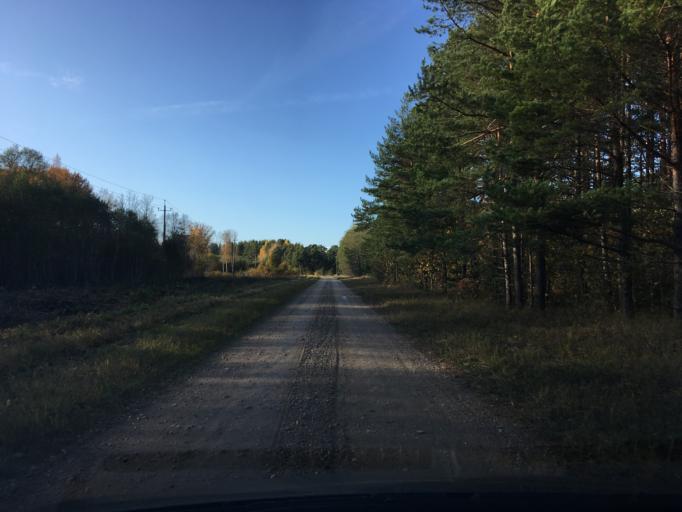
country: EE
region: Laeaene
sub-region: Lihula vald
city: Lihula
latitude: 58.5664
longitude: 23.7660
